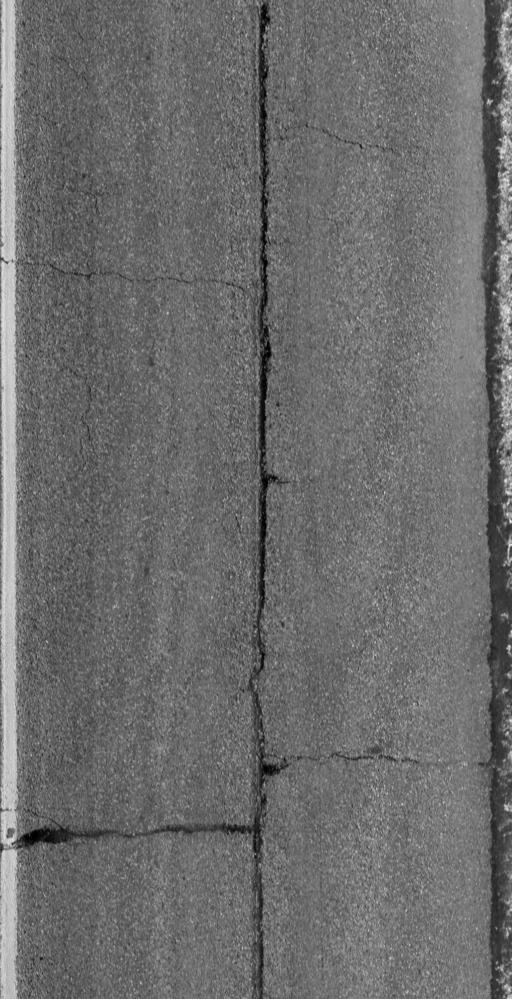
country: US
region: Vermont
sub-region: Chittenden County
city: Milton
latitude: 44.6418
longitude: -73.1003
